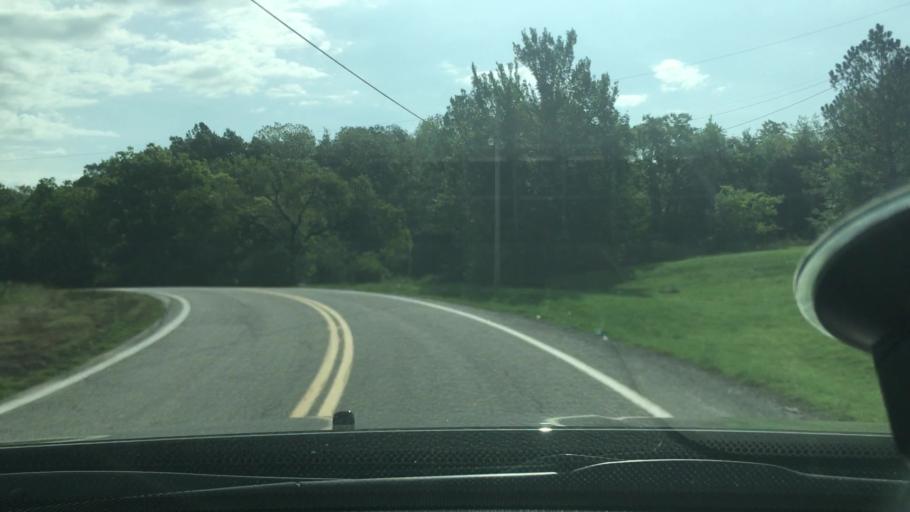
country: US
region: Oklahoma
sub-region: Atoka County
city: Atoka
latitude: 34.4677
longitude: -96.0499
